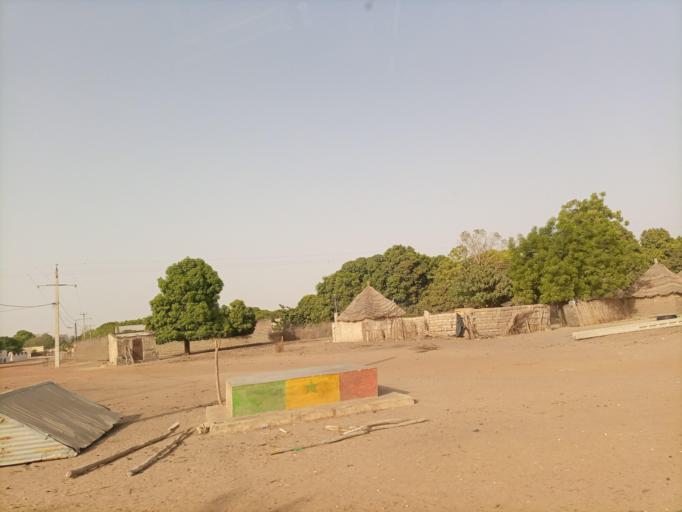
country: SN
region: Fatick
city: Passi
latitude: 14.0190
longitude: -16.2945
